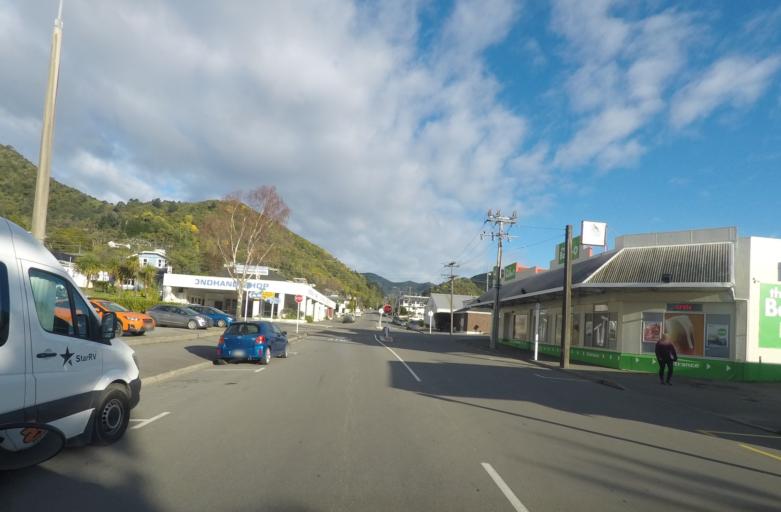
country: NZ
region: Marlborough
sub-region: Marlborough District
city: Picton
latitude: -41.2902
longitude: 174.0080
